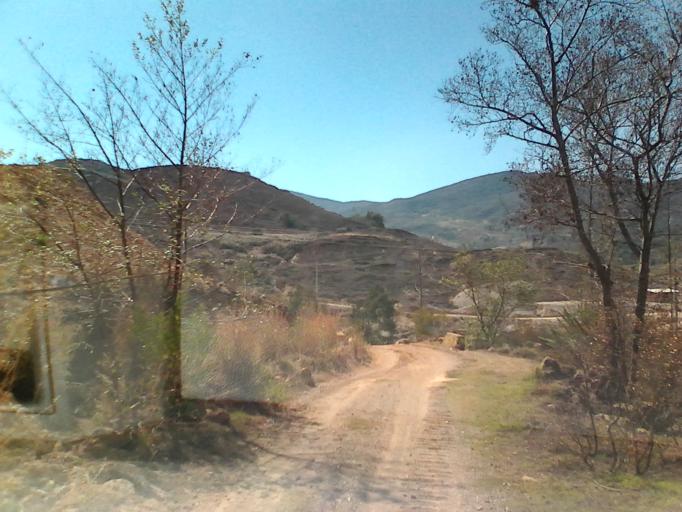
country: CO
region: Boyaca
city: Sachica
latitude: 5.5506
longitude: -73.5634
